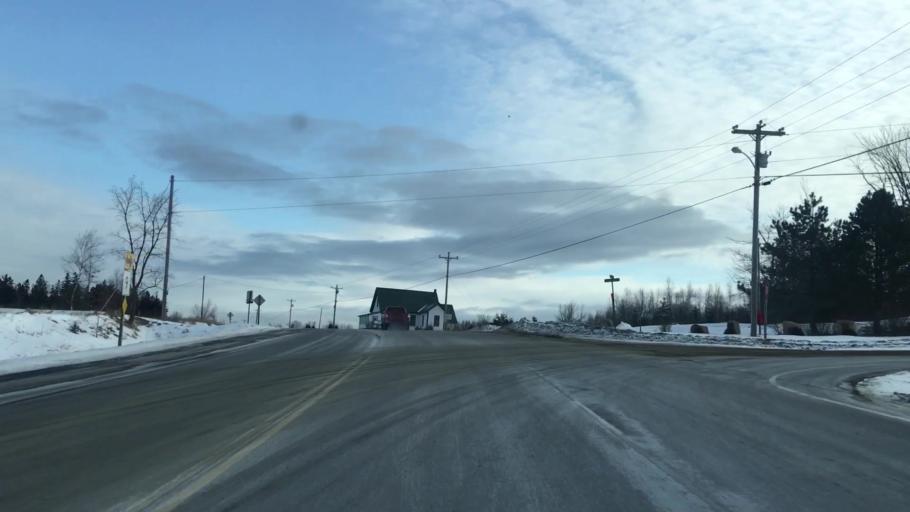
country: US
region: Maine
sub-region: Washington County
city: Machias
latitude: 44.9514
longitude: -67.6642
